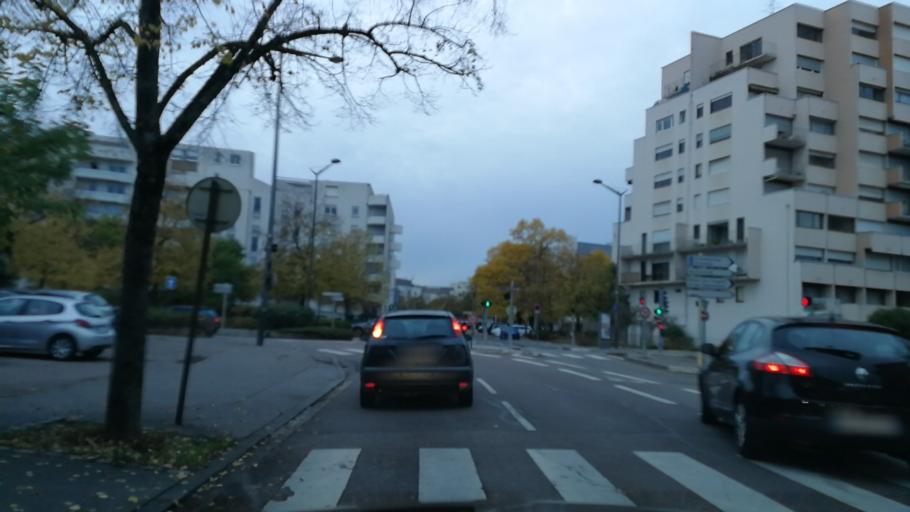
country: FR
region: Bourgogne
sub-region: Departement de la Cote-d'Or
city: Saint-Apollinaire
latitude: 47.3265
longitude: 5.0532
